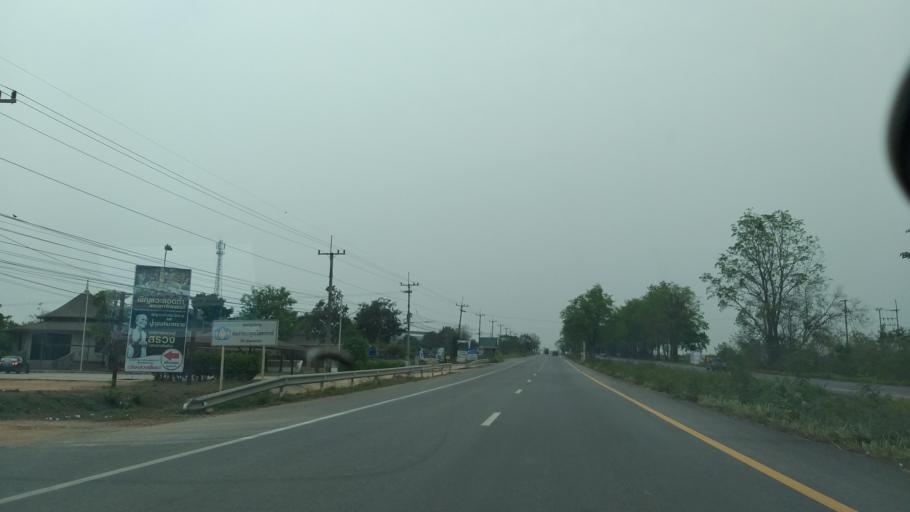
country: TH
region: Chachoengsao
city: Plaeng Yao
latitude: 13.5010
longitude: 101.2712
